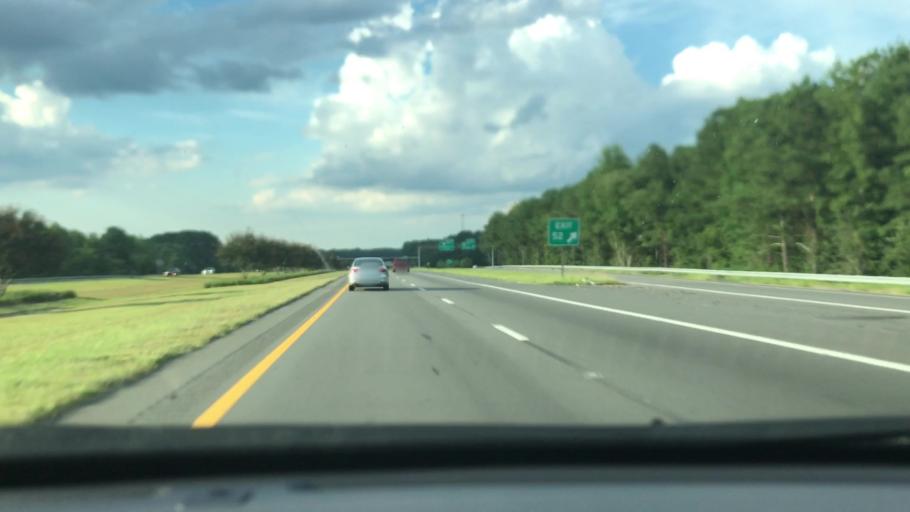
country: US
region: North Carolina
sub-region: Cumberland County
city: Vander
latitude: 35.0360
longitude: -78.8053
